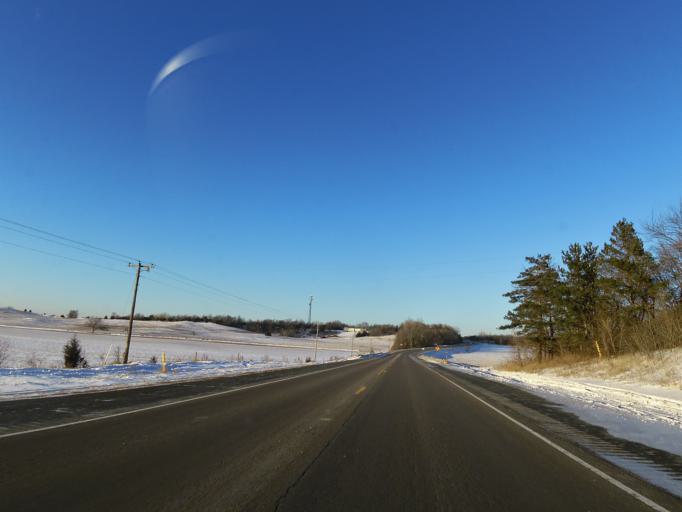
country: US
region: Minnesota
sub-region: Dakota County
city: Farmington
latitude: 44.5528
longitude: -93.1367
